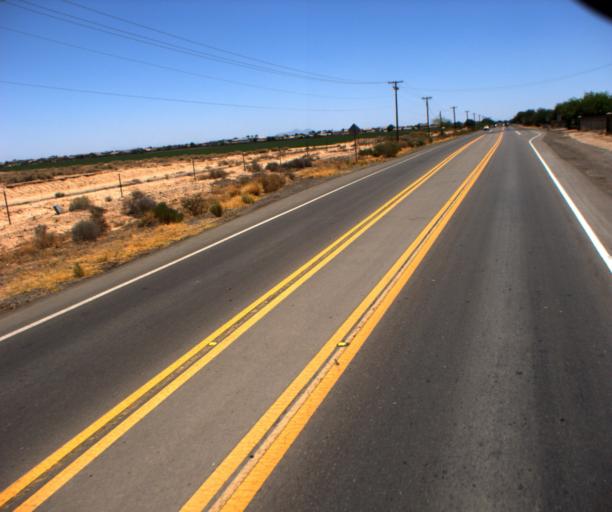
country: US
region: Arizona
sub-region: Pinal County
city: Maricopa
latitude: 33.0724
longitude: -112.0565
